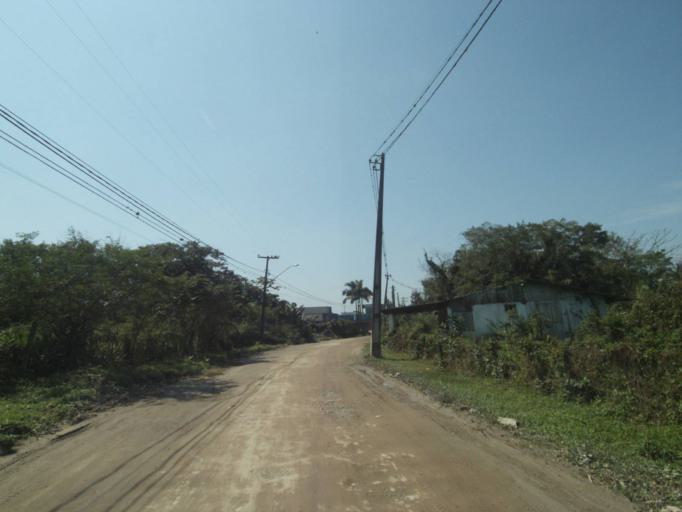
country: BR
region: Parana
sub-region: Paranagua
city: Paranagua
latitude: -25.5601
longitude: -48.6091
